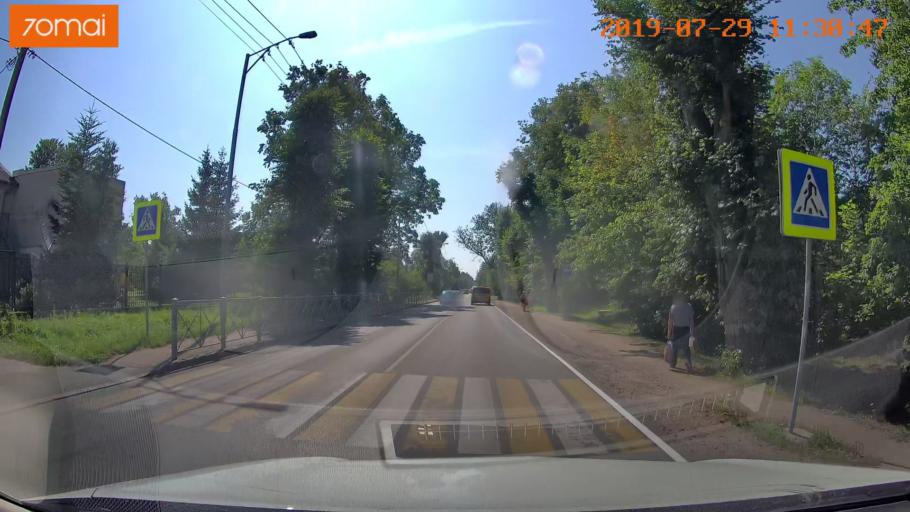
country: RU
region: Kaliningrad
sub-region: Gorod Kaliningrad
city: Kaliningrad
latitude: 54.6799
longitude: 20.5369
